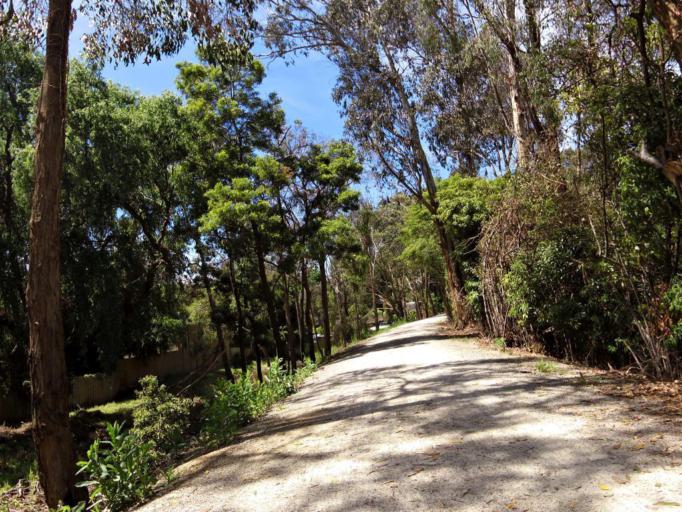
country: AU
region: Victoria
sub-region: Yarra Ranges
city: Mount Evelyn
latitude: -37.7671
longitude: 145.3732
